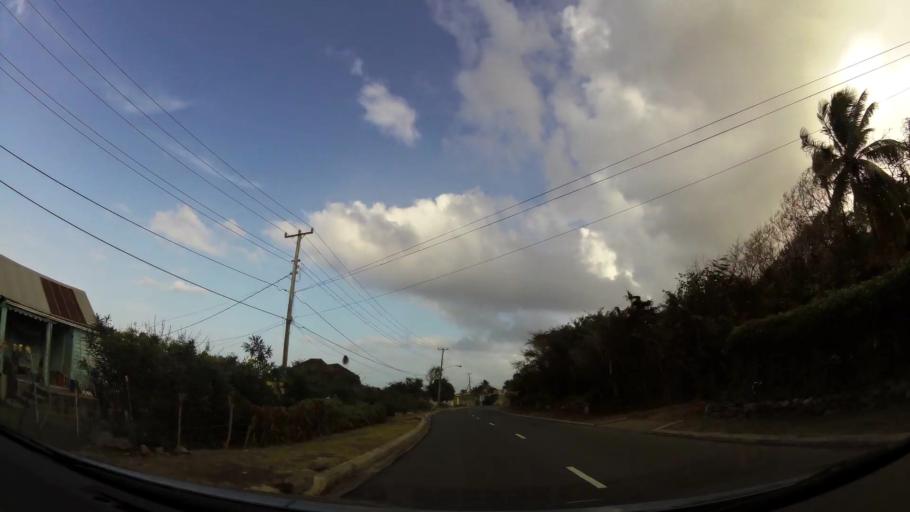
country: KN
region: Saint James Windwa
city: Newcastle
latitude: 17.1960
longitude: -62.5724
